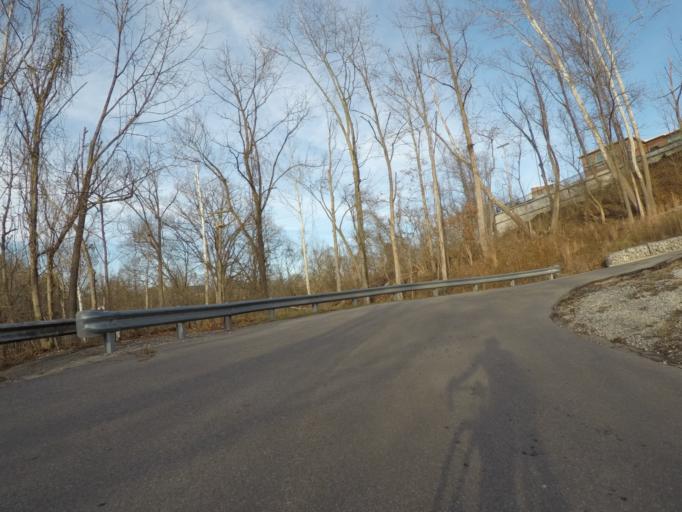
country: US
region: West Virginia
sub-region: Cabell County
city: Huntington
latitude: 38.4074
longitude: -82.3926
